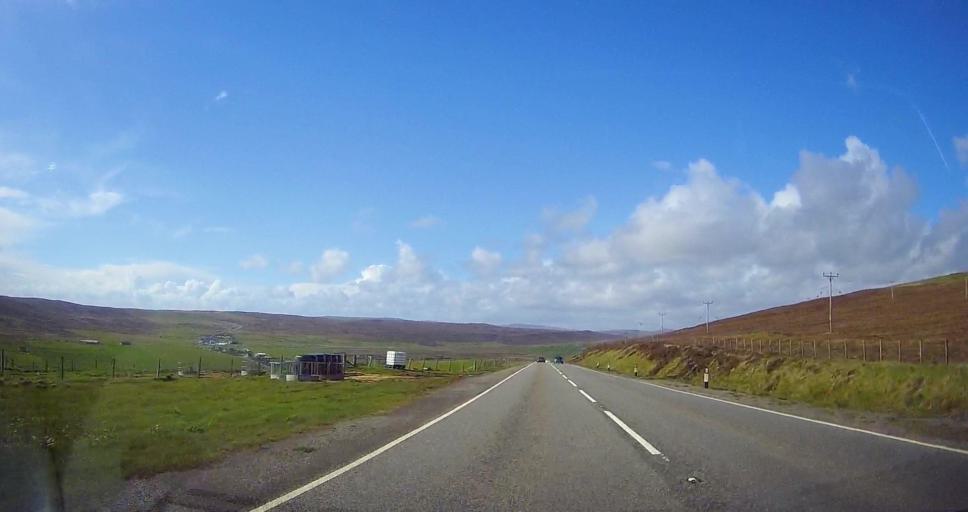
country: GB
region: Scotland
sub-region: Shetland Islands
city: Lerwick
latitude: 60.1766
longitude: -1.2230
